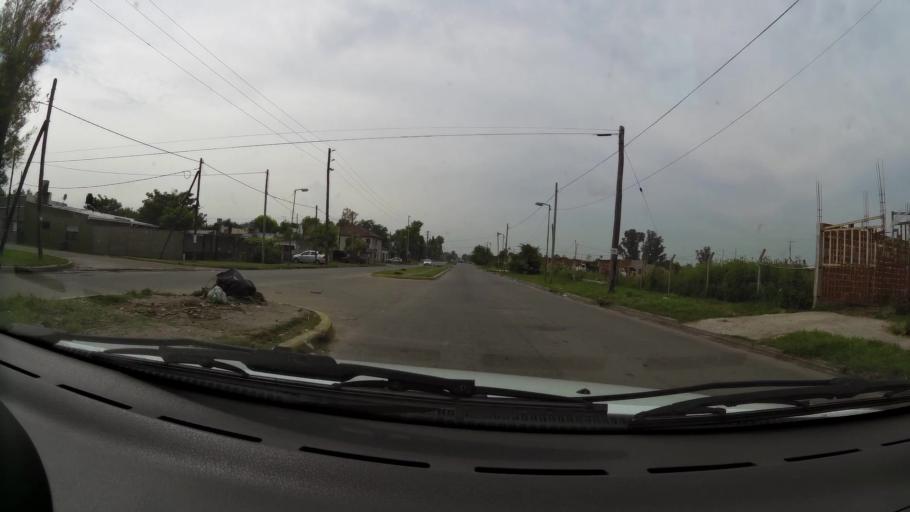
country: AR
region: Buenos Aires
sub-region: Partido de La Plata
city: La Plata
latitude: -34.9266
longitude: -58.0173
